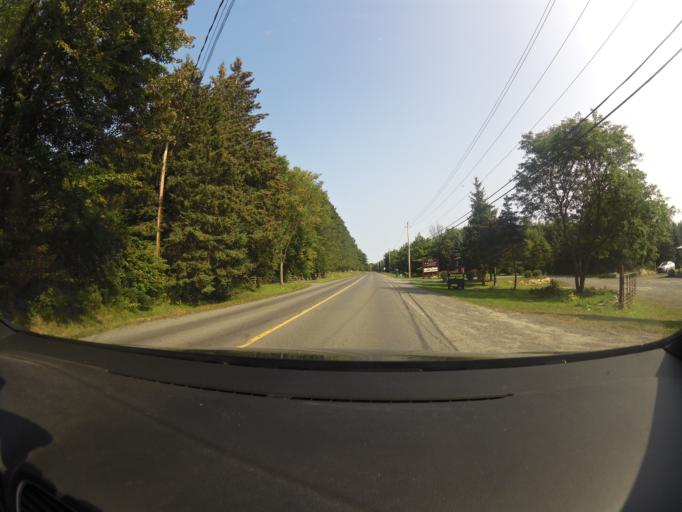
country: CA
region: Ontario
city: Bells Corners
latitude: 45.3440
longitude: -76.0197
